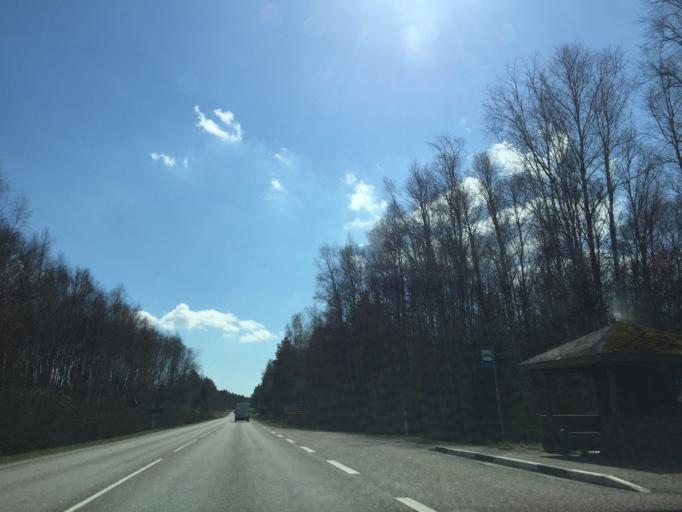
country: EE
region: Tartu
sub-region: Elva linn
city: Elva
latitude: 58.0724
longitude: 26.2047
